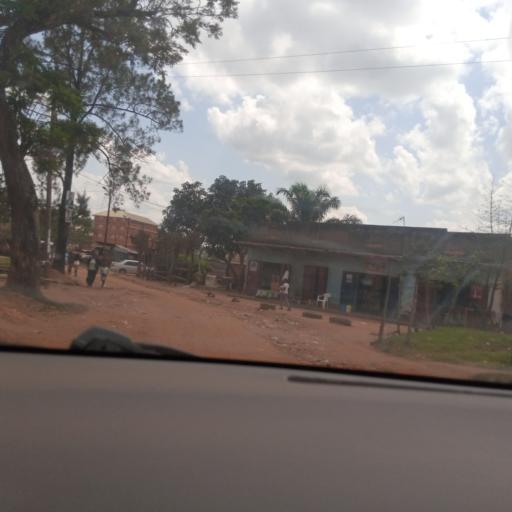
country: UG
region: Central Region
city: Masaka
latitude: -0.3159
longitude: 31.7417
